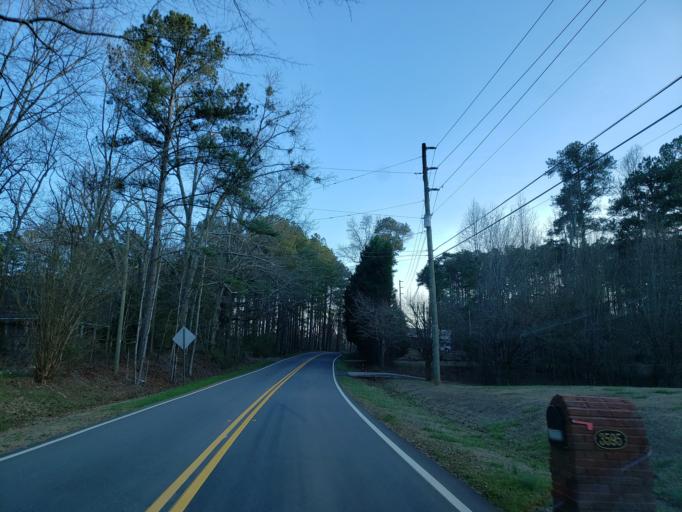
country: US
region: Georgia
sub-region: Cobb County
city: Acworth
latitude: 34.0433
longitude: -84.7282
